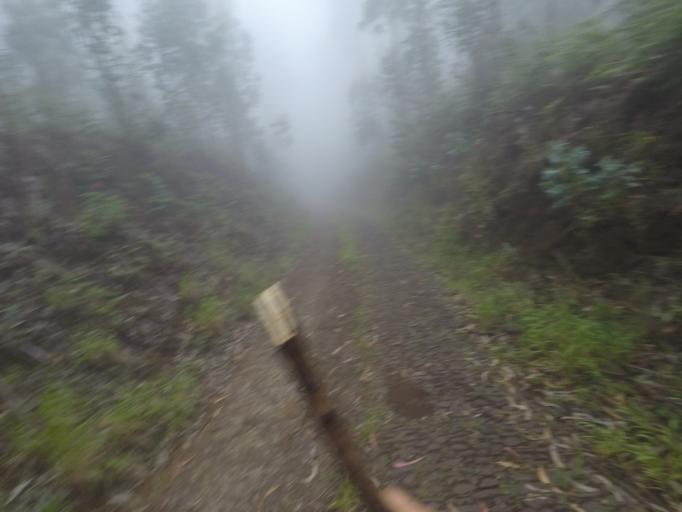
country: PT
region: Madeira
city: Ponta do Sol
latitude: 32.7176
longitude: -17.0935
